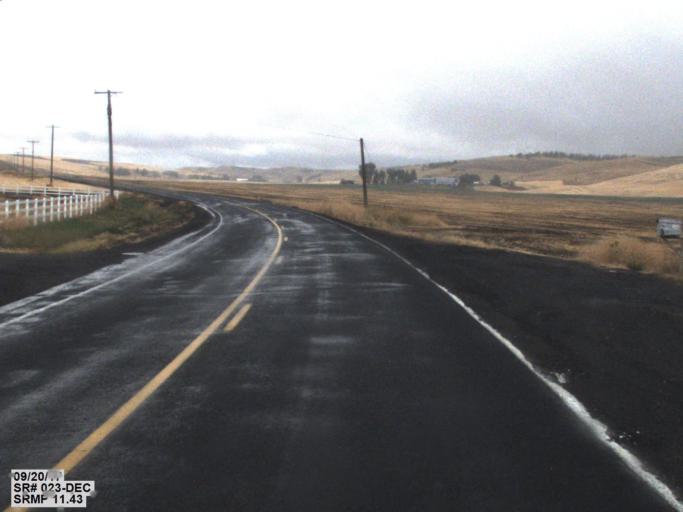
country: US
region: Washington
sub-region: Whitman County
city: Colfax
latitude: 47.0731
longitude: -117.5358
